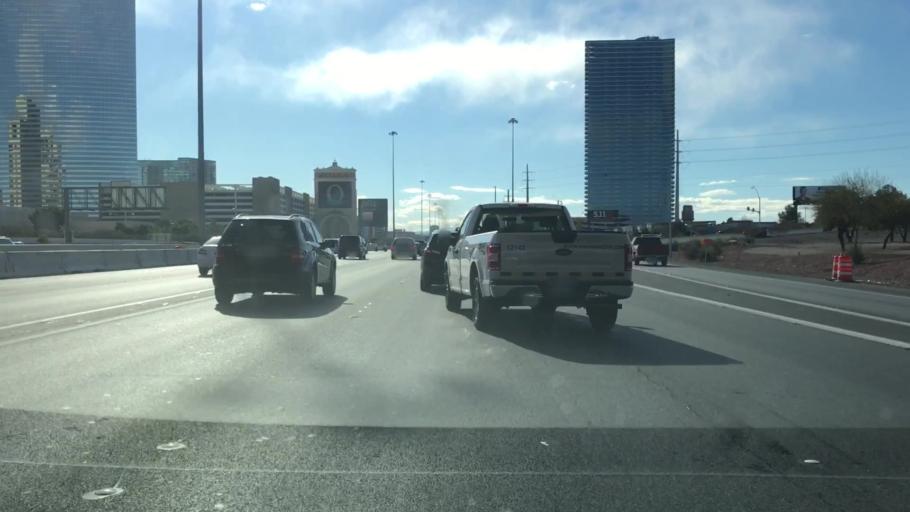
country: US
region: Nevada
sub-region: Clark County
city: Paradise
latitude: 36.1142
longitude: -115.1808
